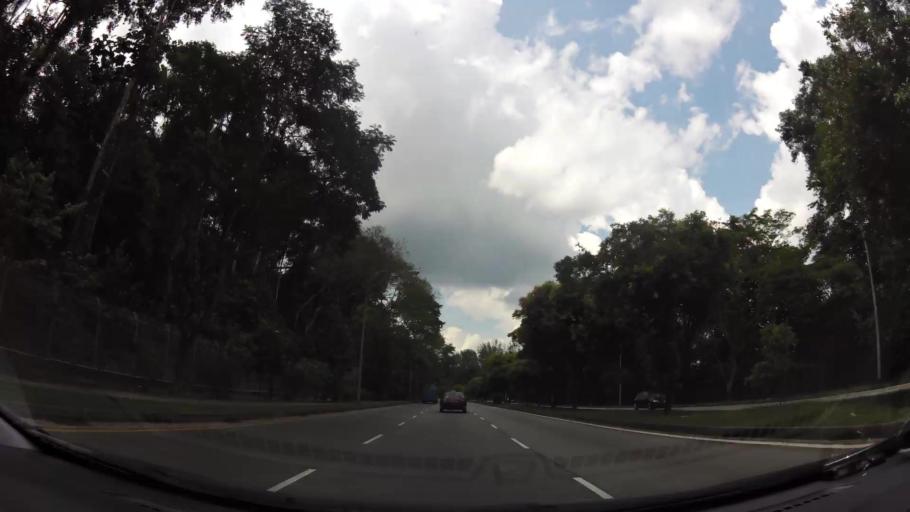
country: MY
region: Johor
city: Johor Bahru
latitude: 1.4145
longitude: 103.8128
